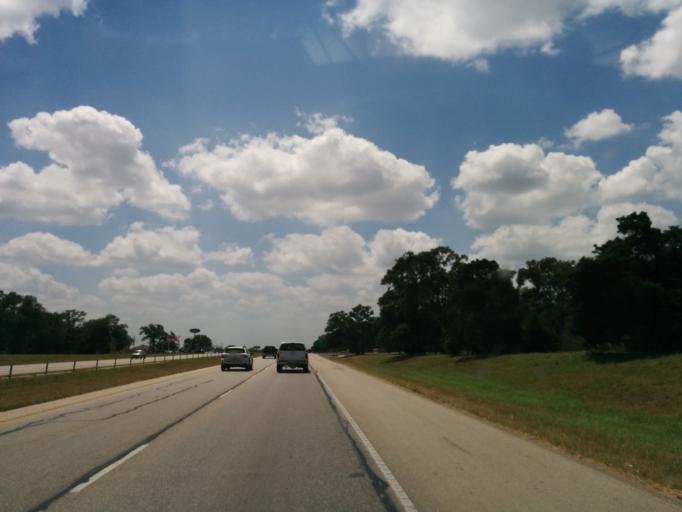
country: US
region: Texas
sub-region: Bastrop County
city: Wyldwood
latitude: 30.1109
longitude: -97.4001
